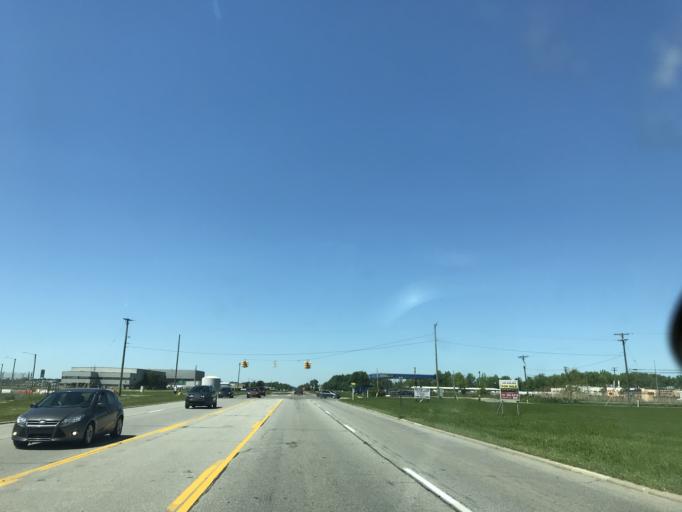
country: US
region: Michigan
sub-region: Wayne County
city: Taylor
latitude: 42.2234
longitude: -83.3273
